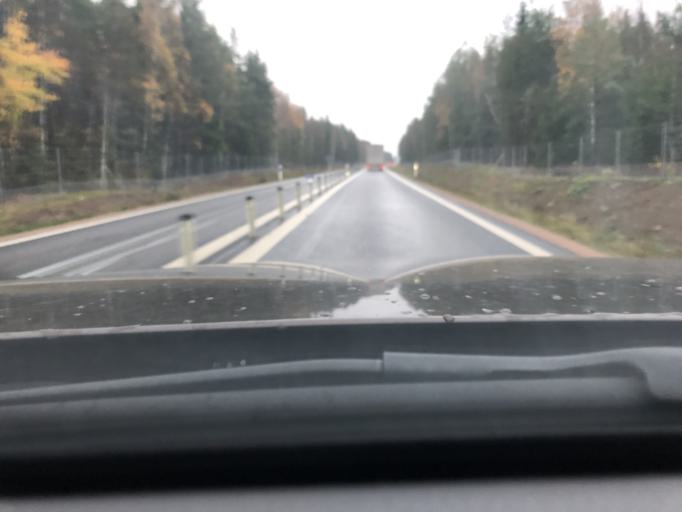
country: SE
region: Kronoberg
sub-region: Almhults Kommun
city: AElmhult
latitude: 56.6406
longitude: 14.2677
